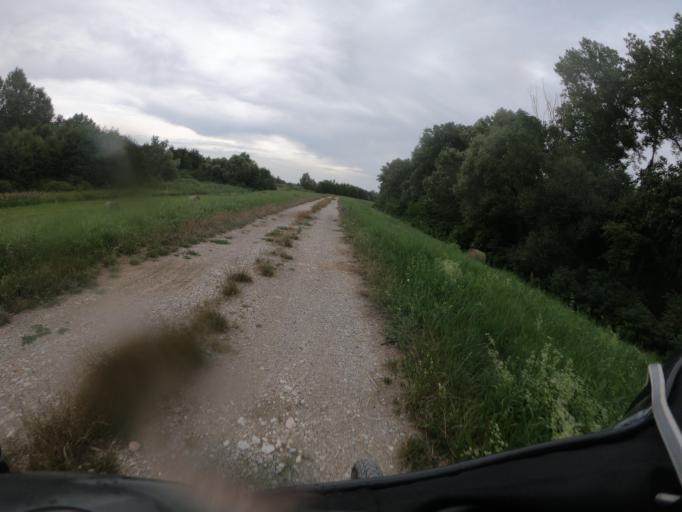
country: HU
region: Jasz-Nagykun-Szolnok
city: Tiszafured
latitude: 47.6776
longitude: 20.7648
